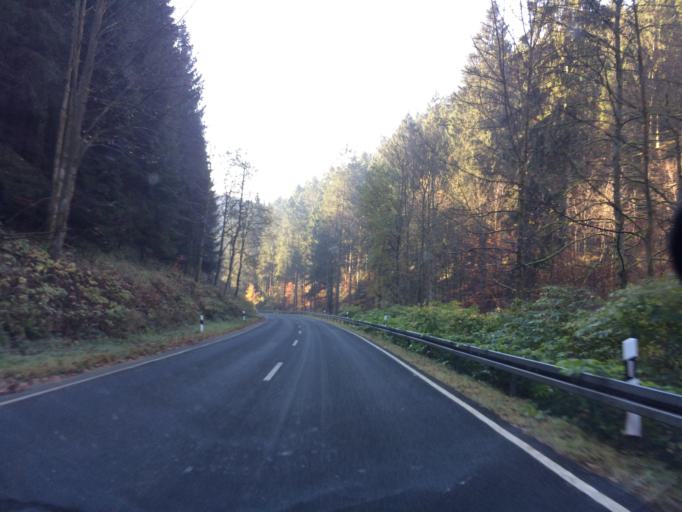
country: DE
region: Lower Saxony
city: Sankt Andreasberg
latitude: 51.7015
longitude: 10.5132
